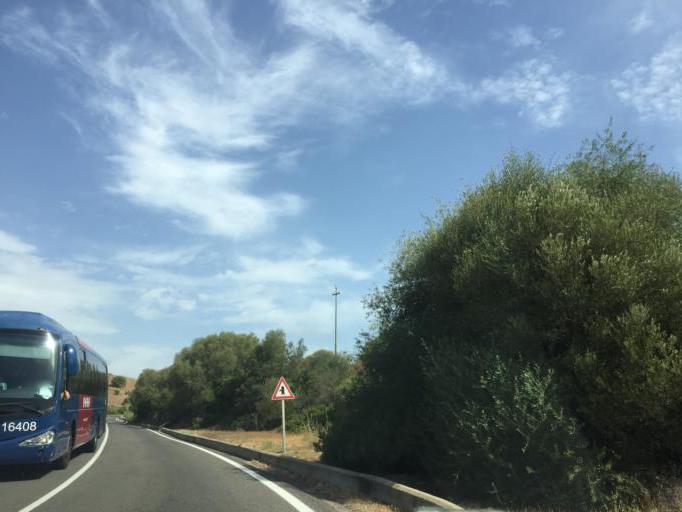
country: IT
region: Sardinia
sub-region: Provincia di Olbia-Tempio
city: San Teodoro
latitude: 40.7324
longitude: 9.6495
